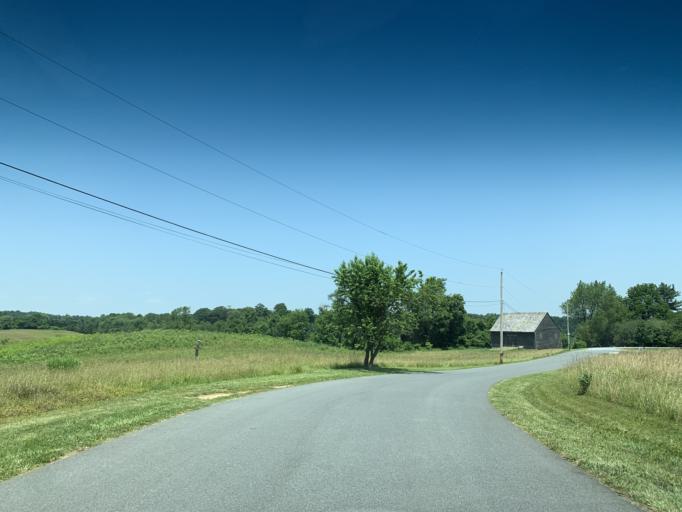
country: US
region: Maryland
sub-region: Howard County
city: Columbia
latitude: 39.3144
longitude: -76.8762
